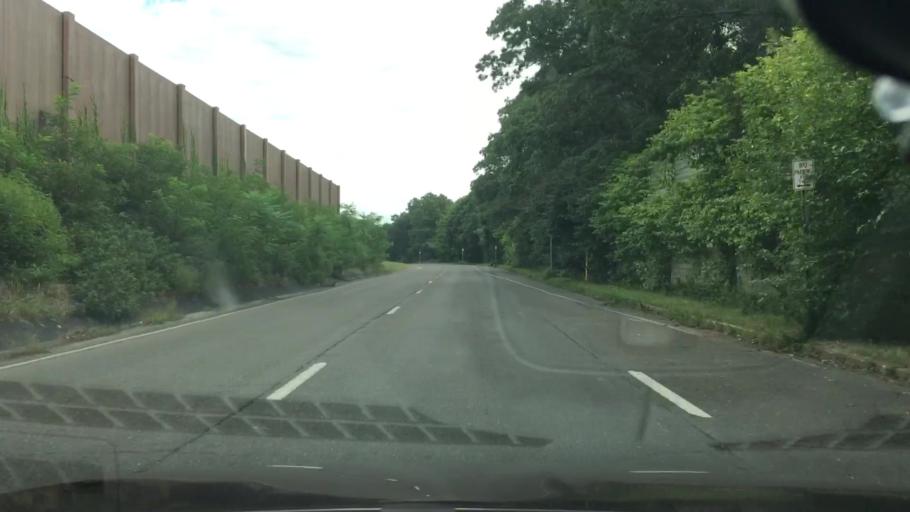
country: US
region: New York
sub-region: Suffolk County
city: Dix Hills
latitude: 40.8021
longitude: -73.3190
